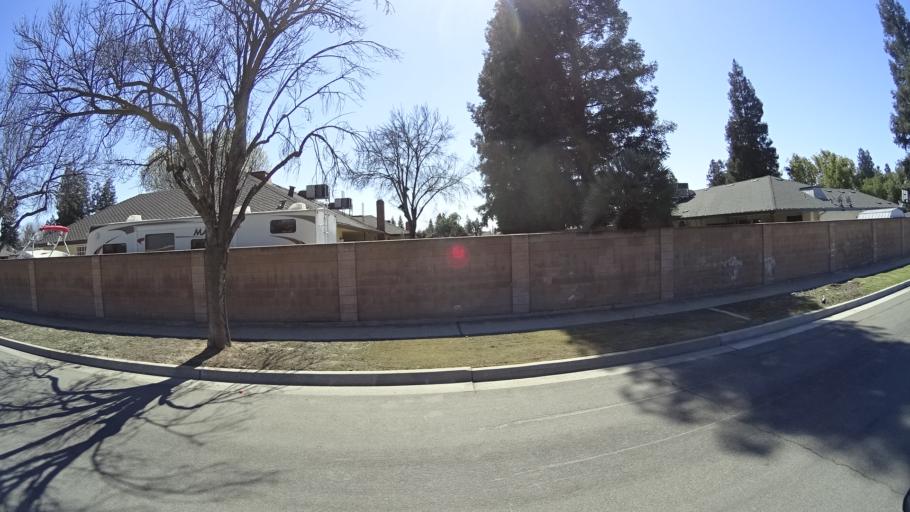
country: US
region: California
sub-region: Fresno County
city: Clovis
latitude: 36.8480
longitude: -119.7512
